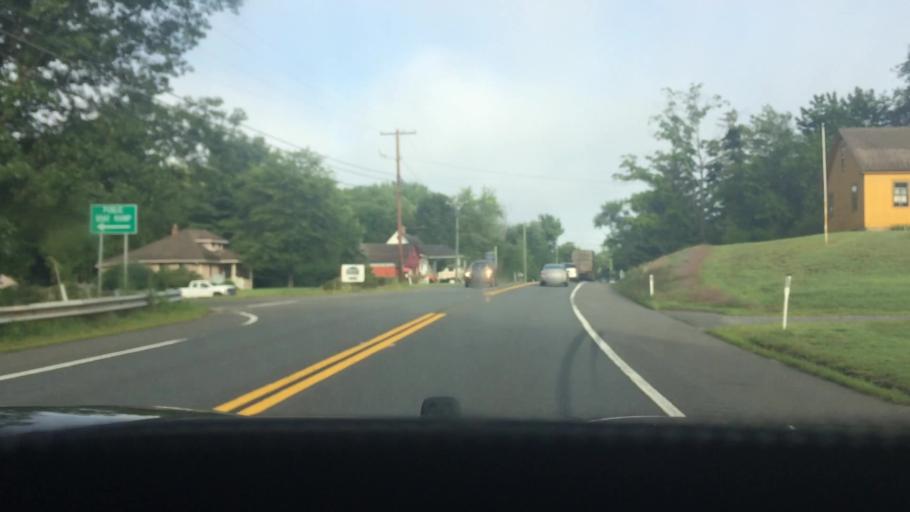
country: US
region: Massachusetts
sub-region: Franklin County
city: Turners Falls
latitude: 42.6094
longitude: -72.5404
